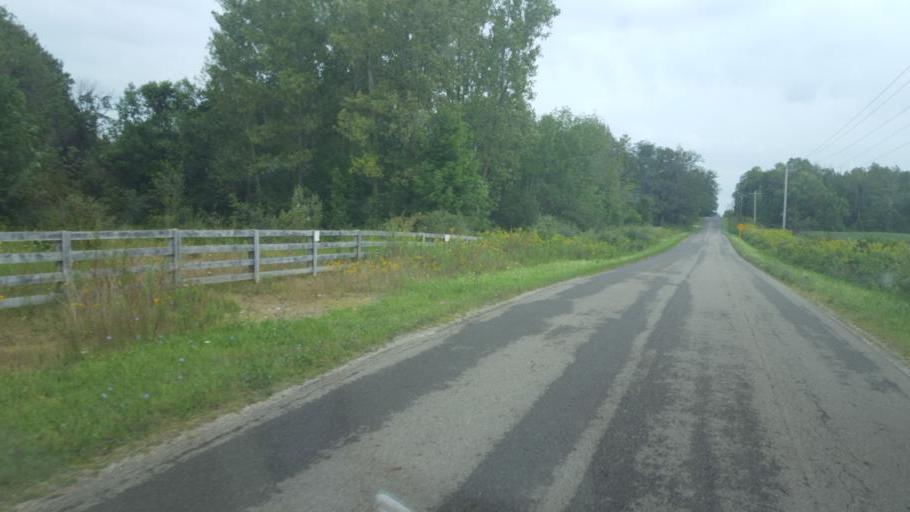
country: US
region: Ohio
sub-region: Morrow County
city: Mount Gilead
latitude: 40.5622
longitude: -82.7333
